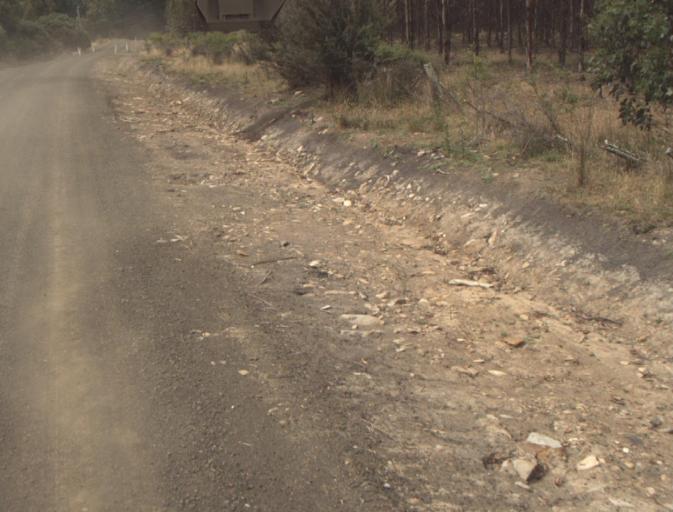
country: AU
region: Tasmania
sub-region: Northern Midlands
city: Evandale
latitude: -41.4514
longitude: 147.4423
